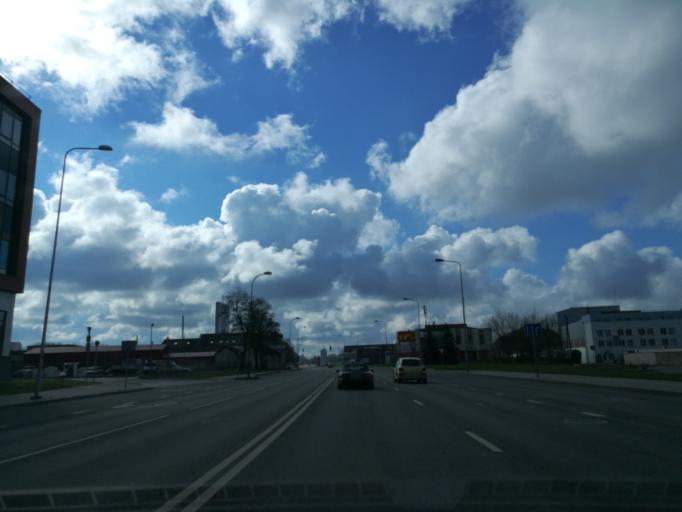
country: LT
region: Klaipedos apskritis
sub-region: Klaipeda
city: Klaipeda
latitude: 55.6978
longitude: 21.1370
